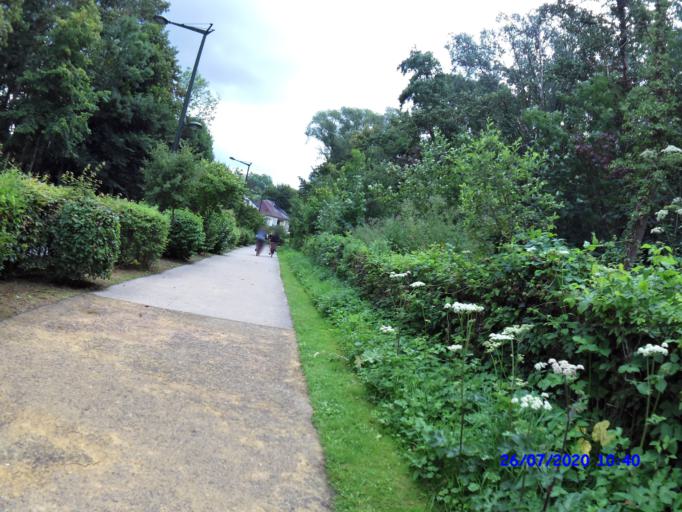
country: BE
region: Flanders
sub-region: Provincie Vlaams-Brabant
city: Drogenbos
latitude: 50.7889
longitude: 4.3351
